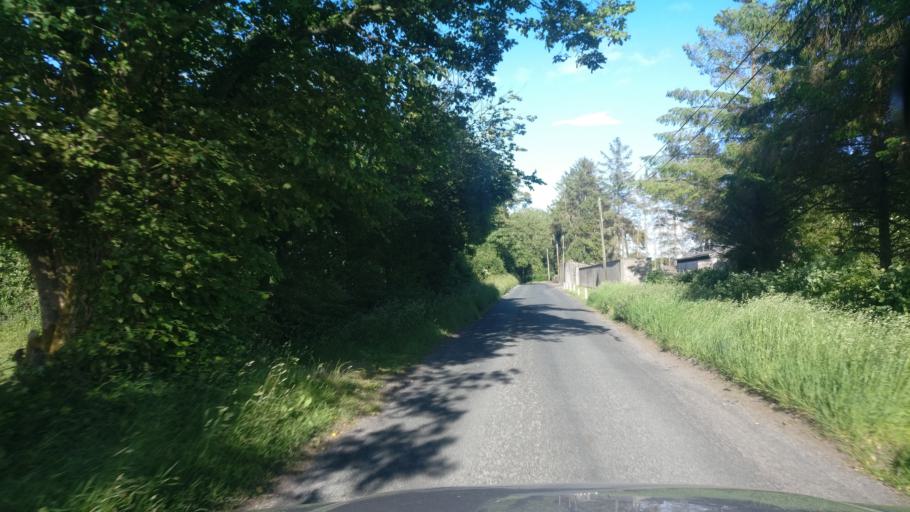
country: IE
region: Connaught
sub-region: County Galway
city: Ballinasloe
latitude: 53.2277
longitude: -8.2347
